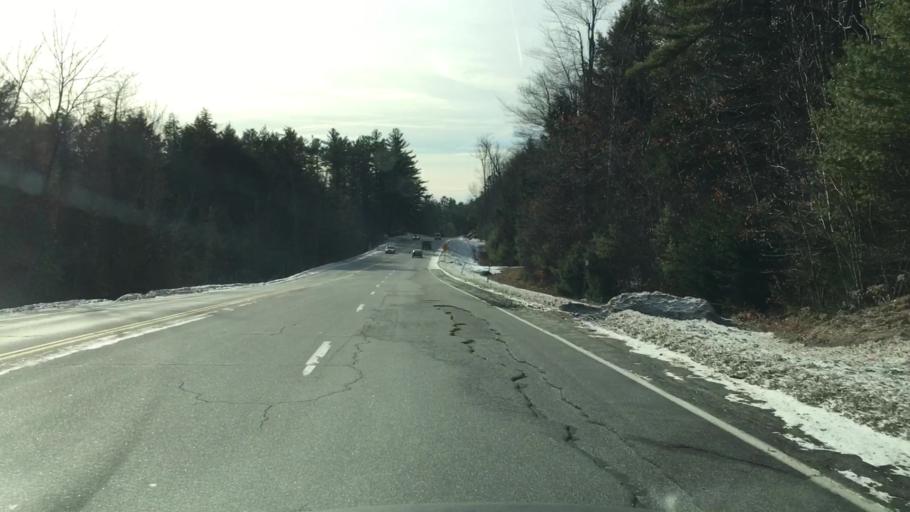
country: US
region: New Hampshire
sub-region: Sullivan County
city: Sunapee
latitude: 43.4228
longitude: -72.0765
